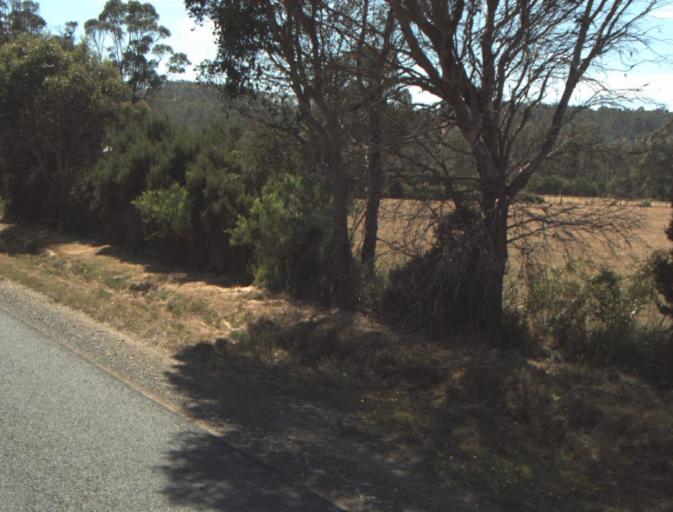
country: AU
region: Tasmania
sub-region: Launceston
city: Mayfield
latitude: -41.2559
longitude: 147.1465
